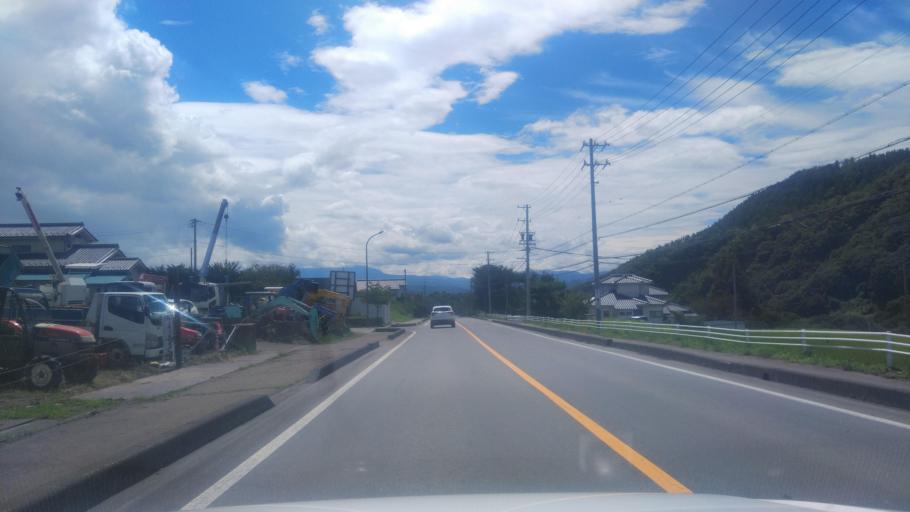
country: JP
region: Nagano
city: Ueda
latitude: 36.4313
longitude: 138.2985
